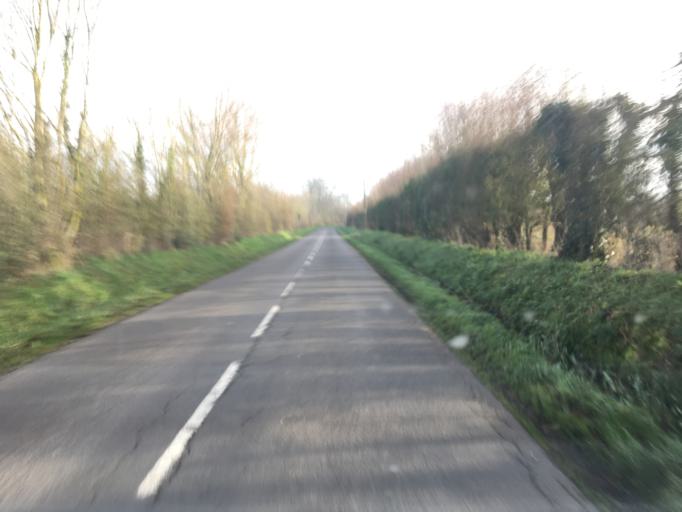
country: FR
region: Lower Normandy
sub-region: Departement du Calvados
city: Dozule
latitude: 49.1949
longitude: -0.0587
